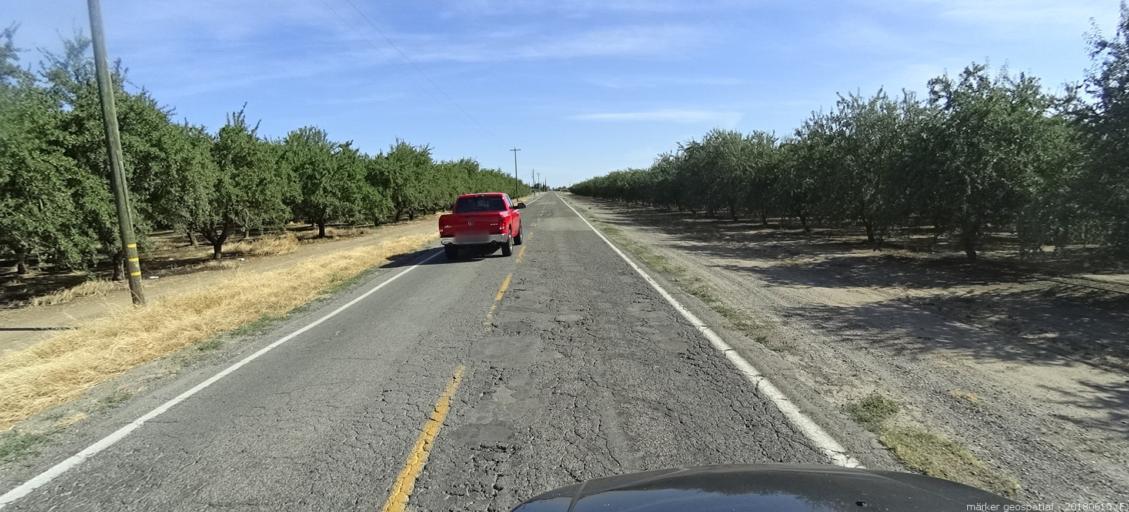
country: US
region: California
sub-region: Madera County
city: Chowchilla
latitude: 37.0628
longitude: -120.2568
